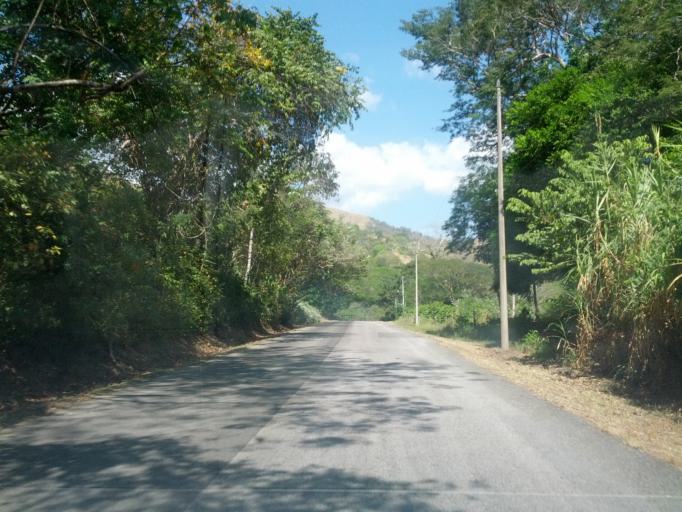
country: CR
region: Puntarenas
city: Buenos Aires
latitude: 8.9631
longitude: -83.3079
